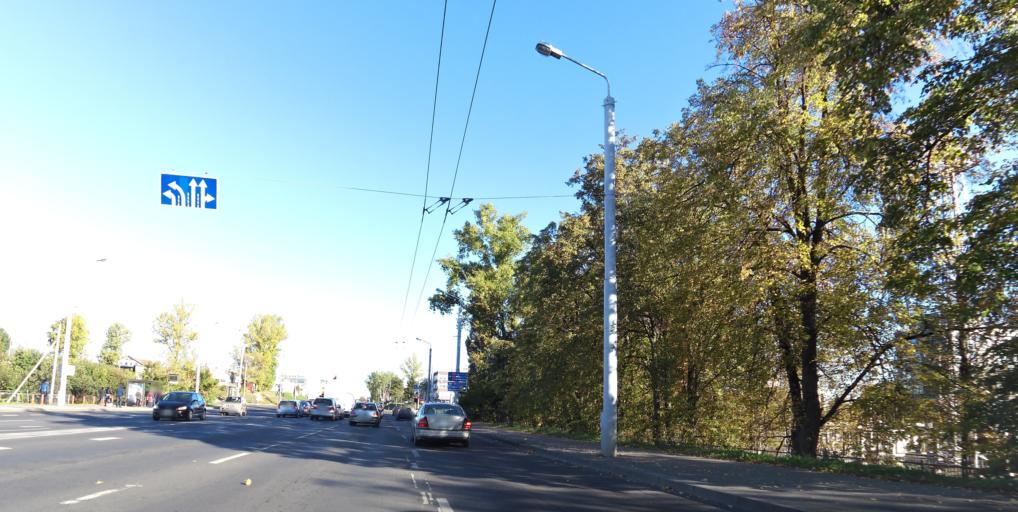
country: LT
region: Vilnius County
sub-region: Vilnius
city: Vilnius
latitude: 54.7139
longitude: 25.2869
